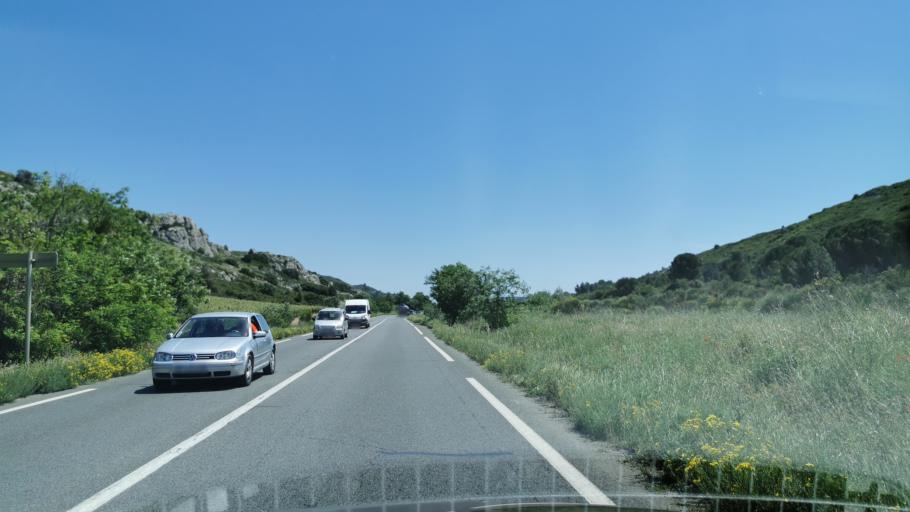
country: FR
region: Languedoc-Roussillon
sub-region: Departement de l'Aude
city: Nevian
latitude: 43.2060
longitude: 2.8858
